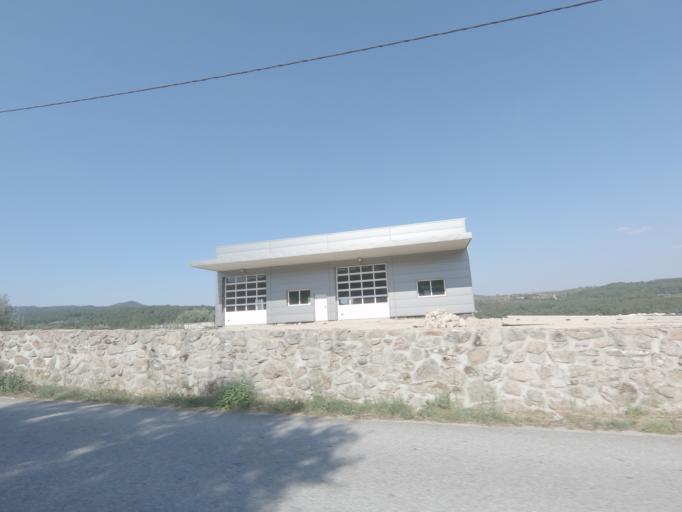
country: PT
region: Viseu
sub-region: Moimenta da Beira
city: Moimenta da Beira
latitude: 40.9762
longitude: -7.5917
